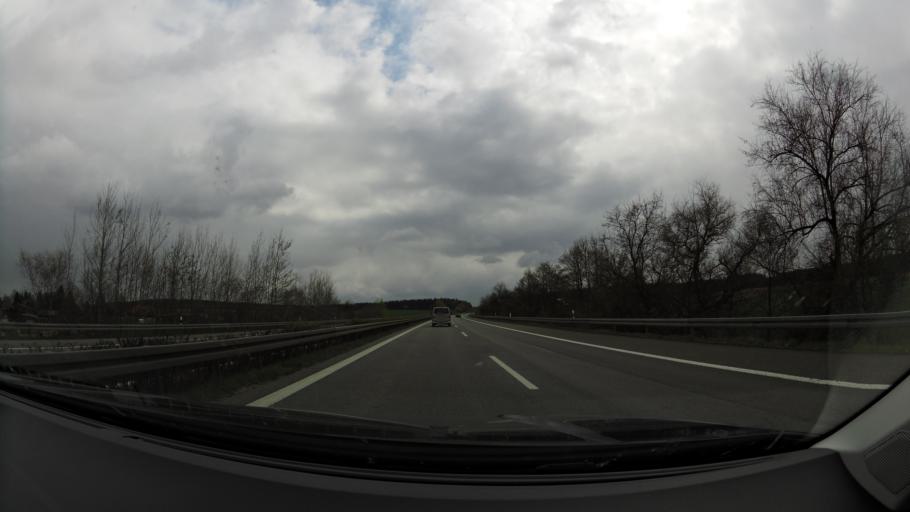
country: DE
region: Mecklenburg-Vorpommern
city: Malchow
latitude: 53.4338
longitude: 12.4162
